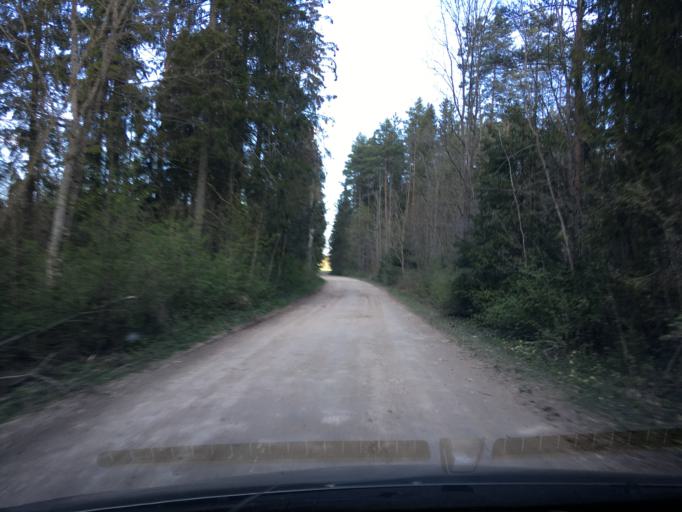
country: EE
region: Harju
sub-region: Raasiku vald
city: Raasiku
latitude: 59.2127
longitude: 25.1681
